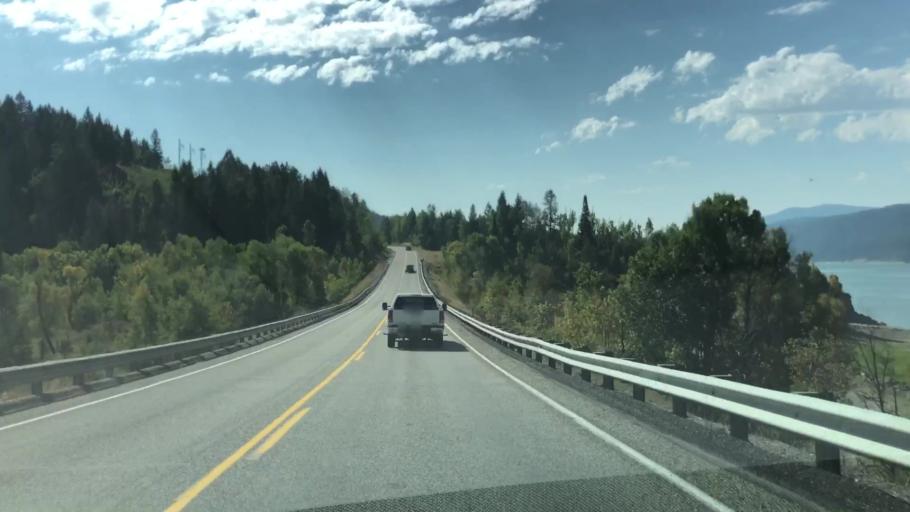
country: US
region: Idaho
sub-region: Teton County
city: Victor
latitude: 43.2845
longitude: -111.1202
